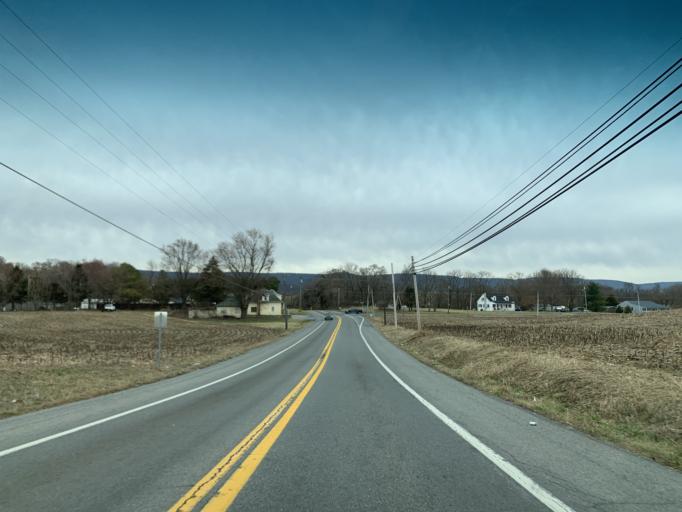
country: US
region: West Virginia
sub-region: Jefferson County
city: Charles Town
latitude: 39.2629
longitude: -77.8328
